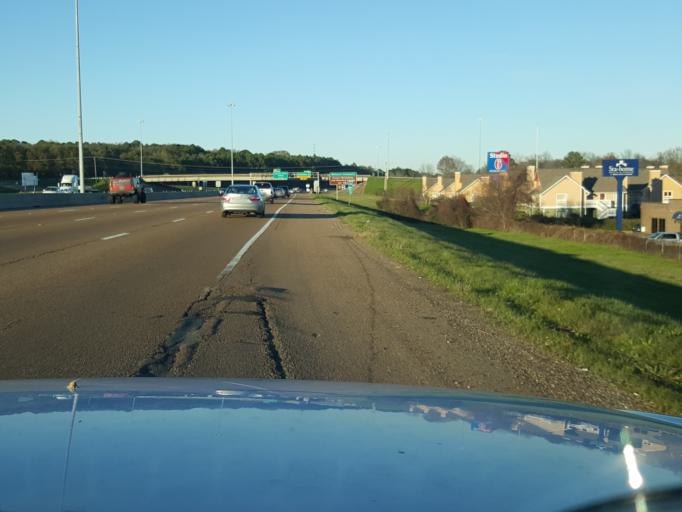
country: US
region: Mississippi
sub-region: Hinds County
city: Jackson
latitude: 32.3065
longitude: -90.1648
